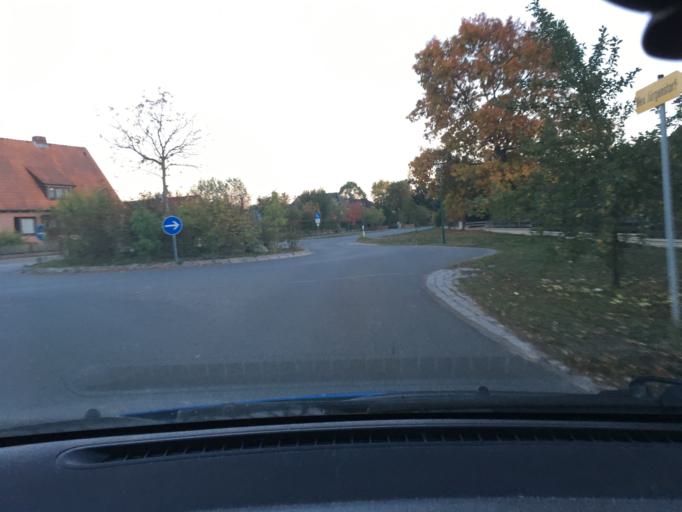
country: DE
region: Lower Saxony
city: Neetze
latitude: 53.2728
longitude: 10.6215
